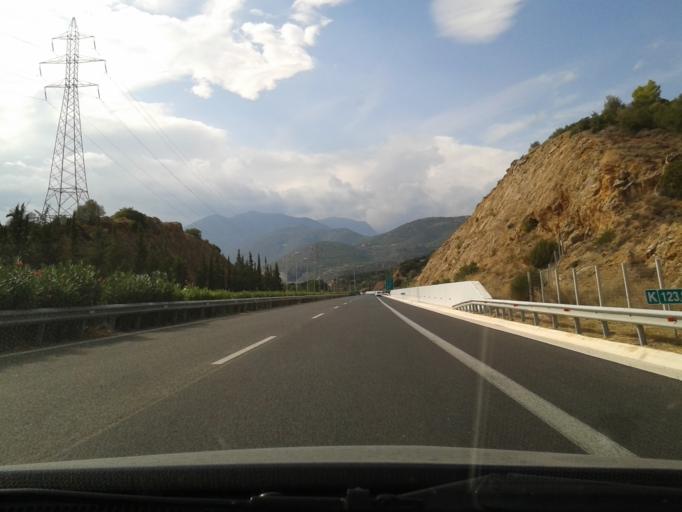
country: GR
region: Peloponnese
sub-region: Nomos Korinthias
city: Nemea
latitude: 37.7229
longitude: 22.6079
